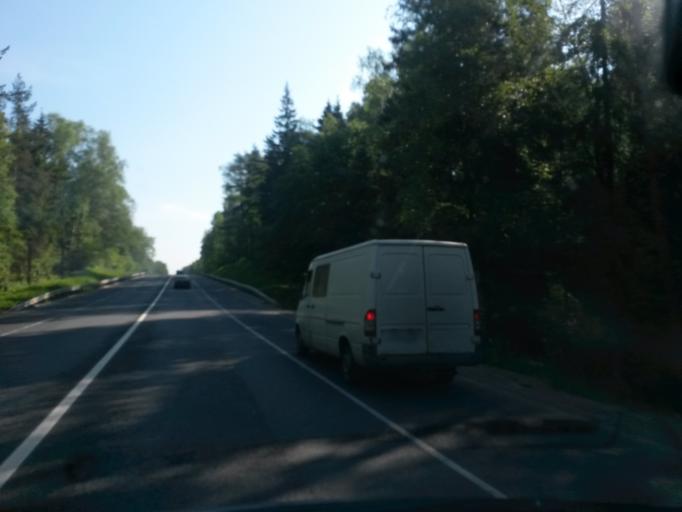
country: RU
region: Jaroslavl
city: Pereslavl'-Zalesskiy
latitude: 56.8558
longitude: 38.9410
